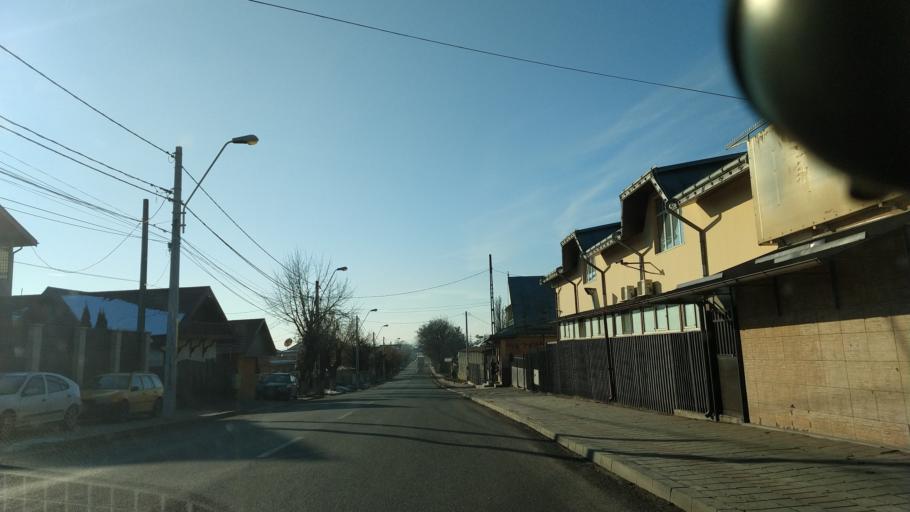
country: RO
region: Neamt
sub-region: Municipiul Roman
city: Roman
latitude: 46.9295
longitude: 26.9154
